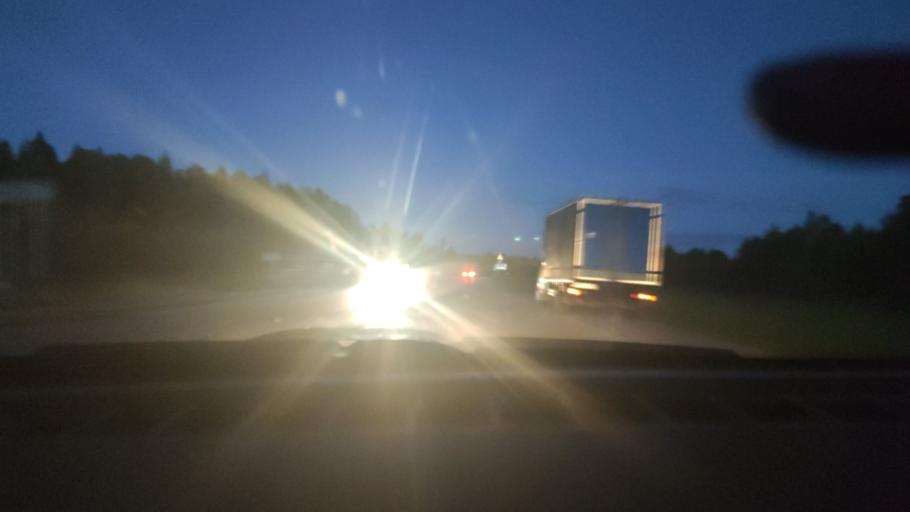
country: RU
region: Perm
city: Polazna
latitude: 58.1112
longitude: 56.4264
